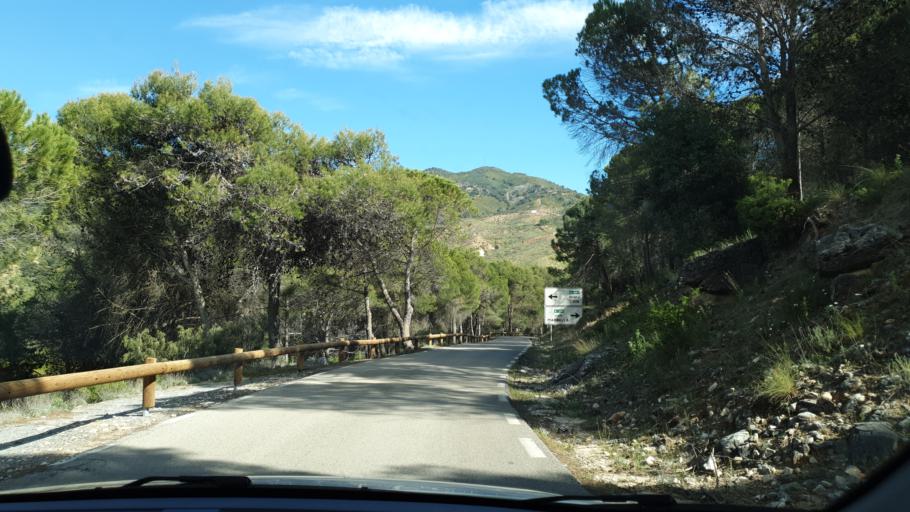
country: ES
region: Andalusia
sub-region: Provincia de Malaga
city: Ojen
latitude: 36.5934
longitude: -4.8557
